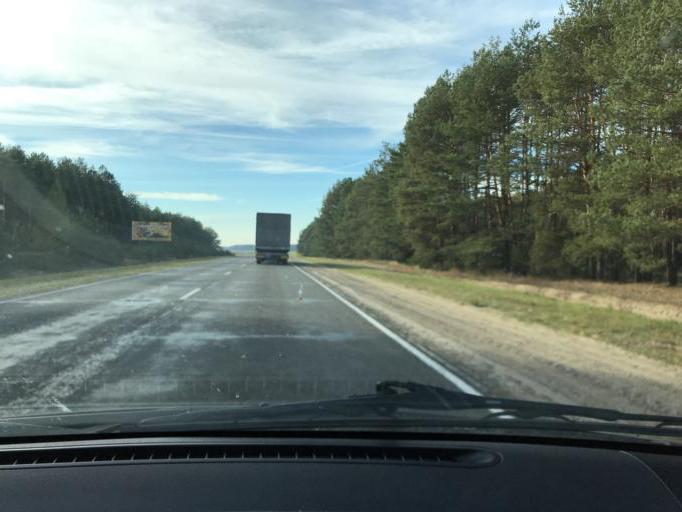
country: BY
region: Brest
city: Horad Pinsk
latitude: 52.1520
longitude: 25.8340
